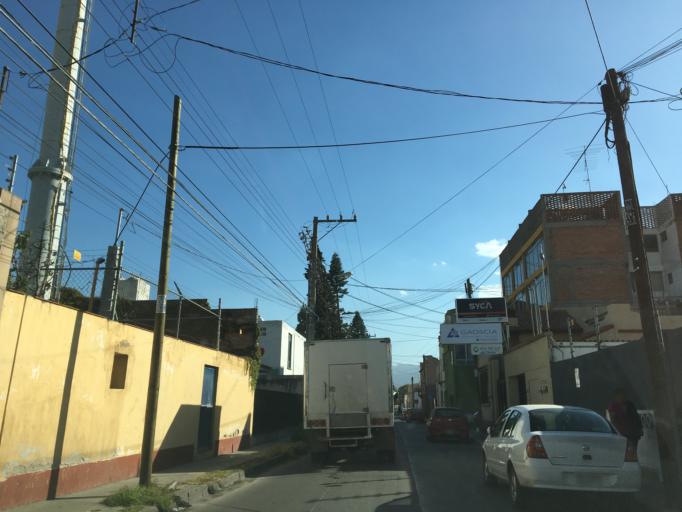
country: MX
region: San Luis Potosi
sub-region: San Luis Potosi
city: San Luis Potosi
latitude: 22.1498
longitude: -100.9930
